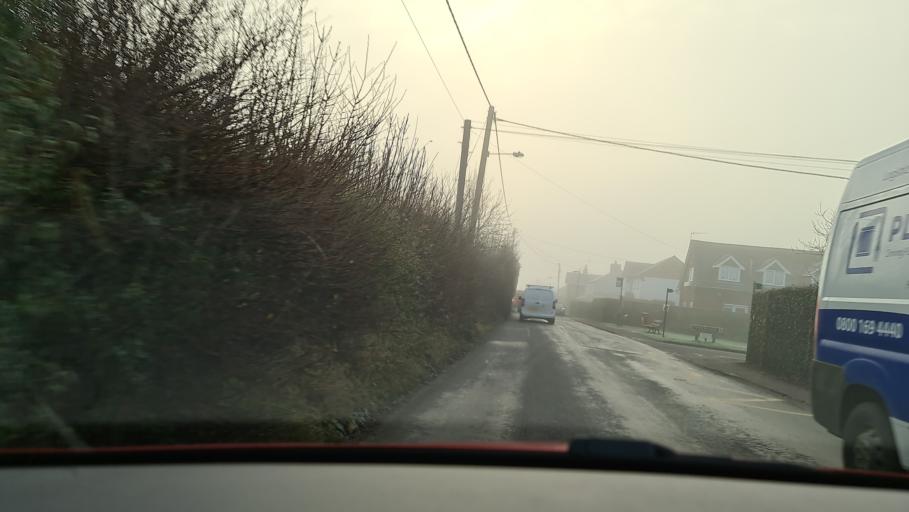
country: GB
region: England
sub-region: Buckinghamshire
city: Waddesdon
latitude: 51.8486
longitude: -0.9600
